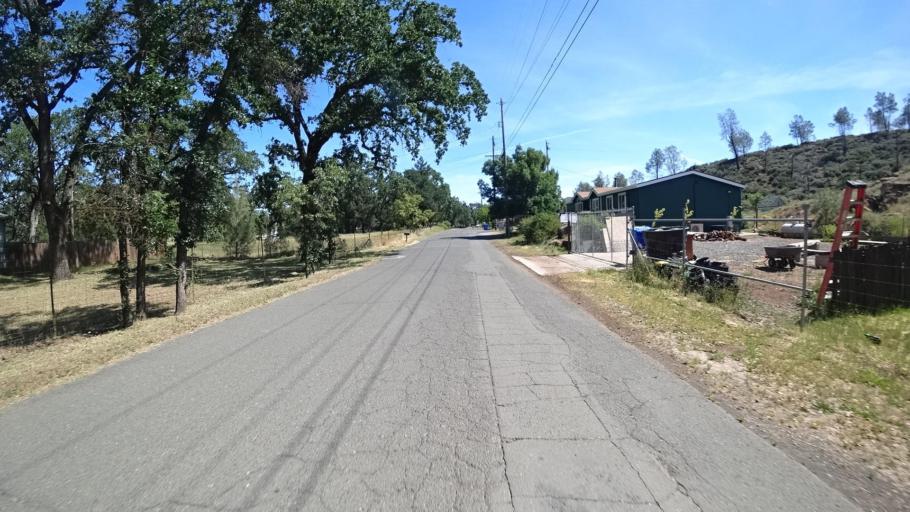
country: US
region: California
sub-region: Lake County
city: Middletown
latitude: 38.7506
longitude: -122.6222
